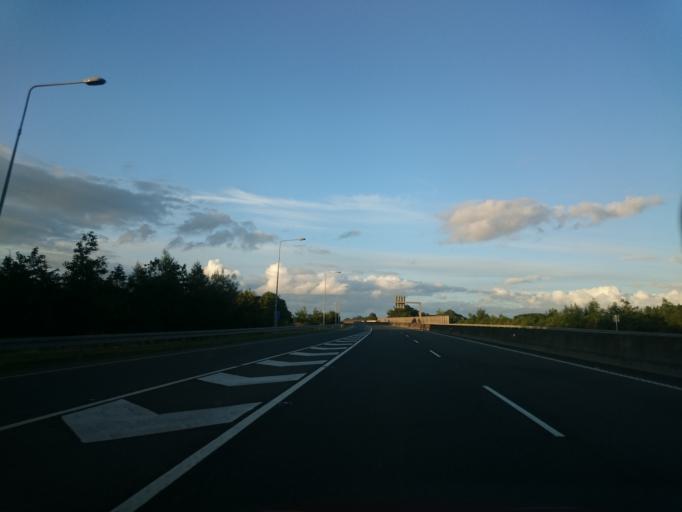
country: IE
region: Leinster
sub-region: Loch Garman
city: Gorey
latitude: 52.6649
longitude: -6.2689
